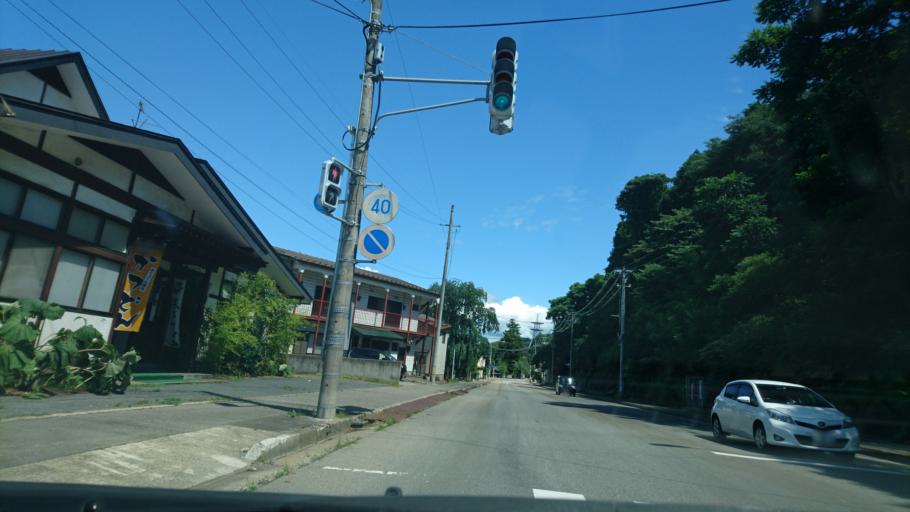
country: JP
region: Akita
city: Kakunodatemachi
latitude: 39.5885
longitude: 140.5653
